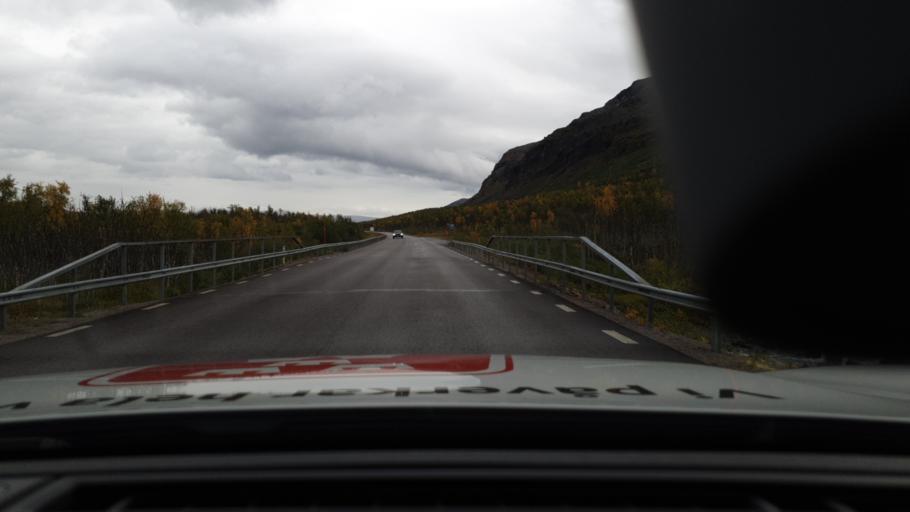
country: NO
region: Troms
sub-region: Bardu
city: Setermoen
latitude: 68.4259
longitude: 18.3517
